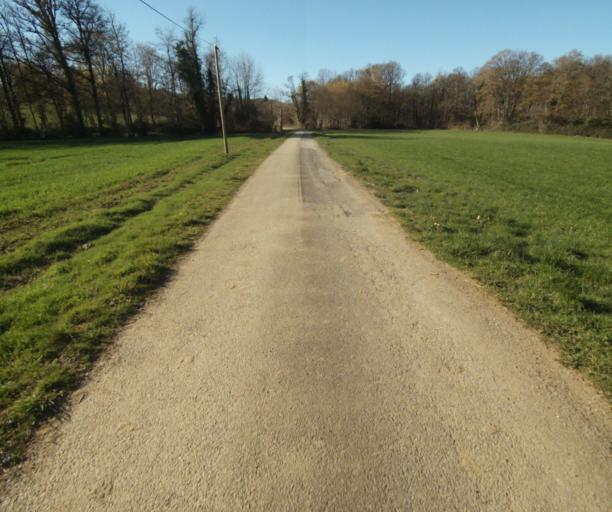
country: FR
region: Limousin
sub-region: Departement de la Correze
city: Seilhac
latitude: 45.3877
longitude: 1.7336
